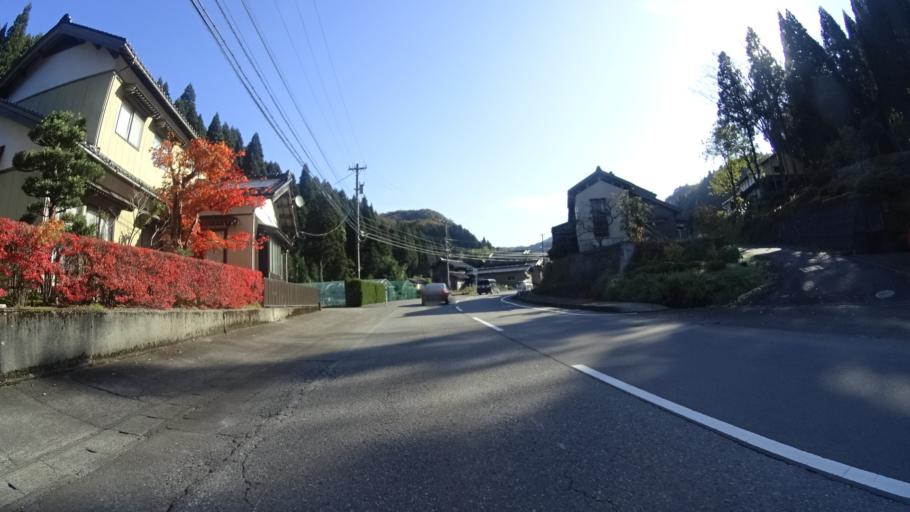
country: JP
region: Ishikawa
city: Komatsu
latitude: 36.3737
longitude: 136.5500
